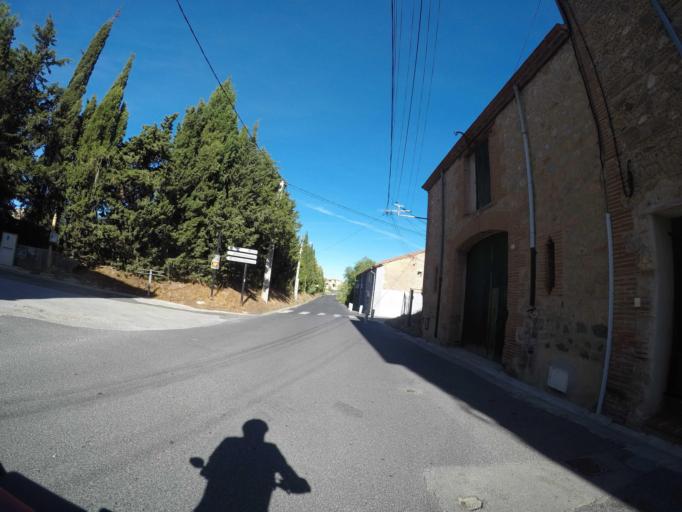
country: FR
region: Languedoc-Roussillon
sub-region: Departement des Pyrenees-Orientales
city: Ponteilla
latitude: 42.6275
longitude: 2.8128
